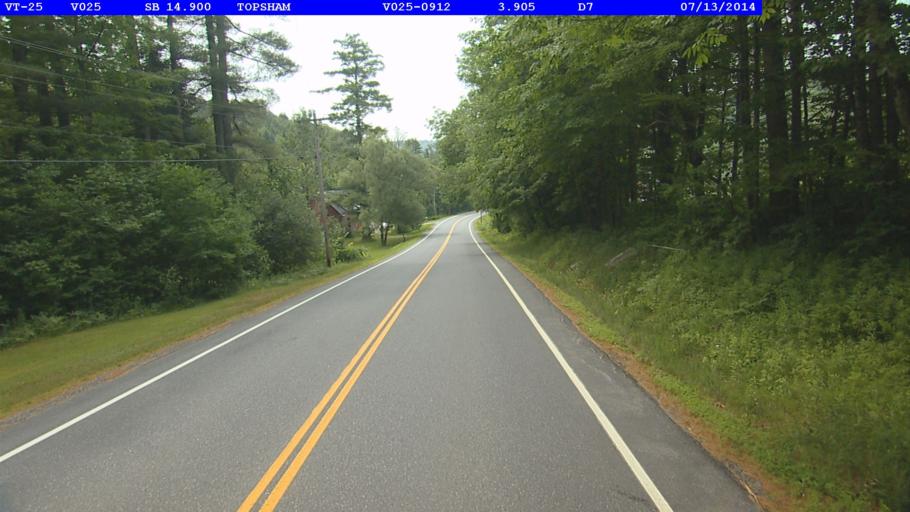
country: US
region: Vermont
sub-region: Orange County
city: Chelsea
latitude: 44.1067
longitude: -72.3188
